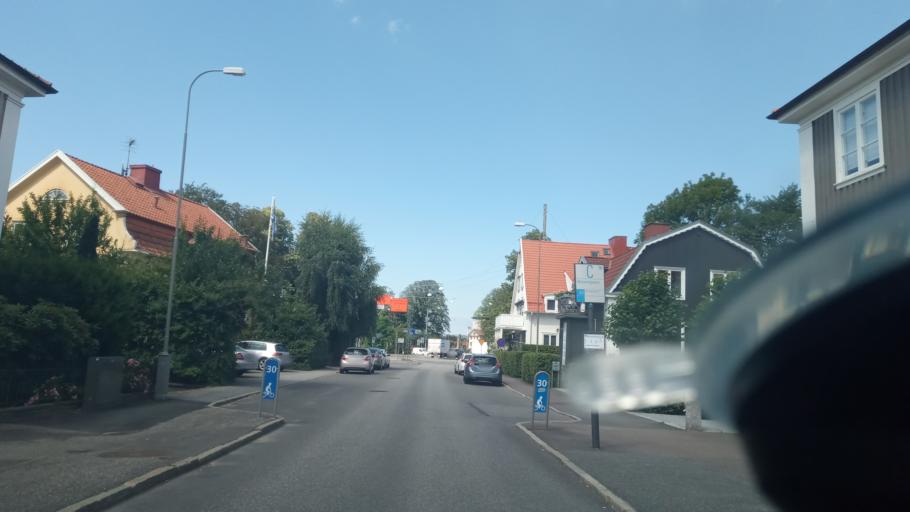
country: SE
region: Vaestra Goetaland
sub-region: Goteborg
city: Goeteborg
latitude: 57.6973
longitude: 12.0005
